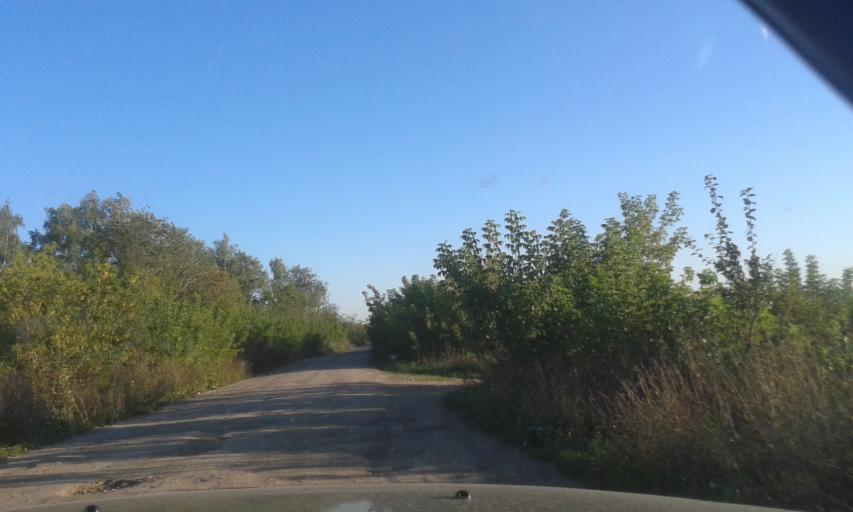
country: RU
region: Tula
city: Krapivna
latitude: 54.1334
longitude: 37.1572
